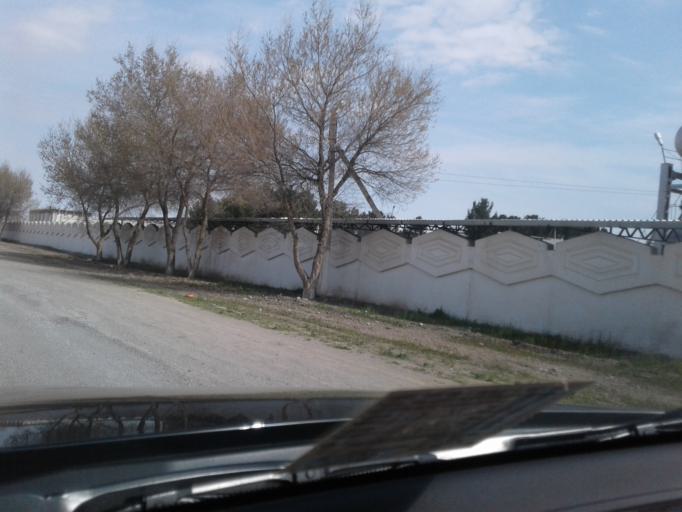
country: TM
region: Ahal
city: Abadan
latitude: 38.1226
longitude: 58.3455
